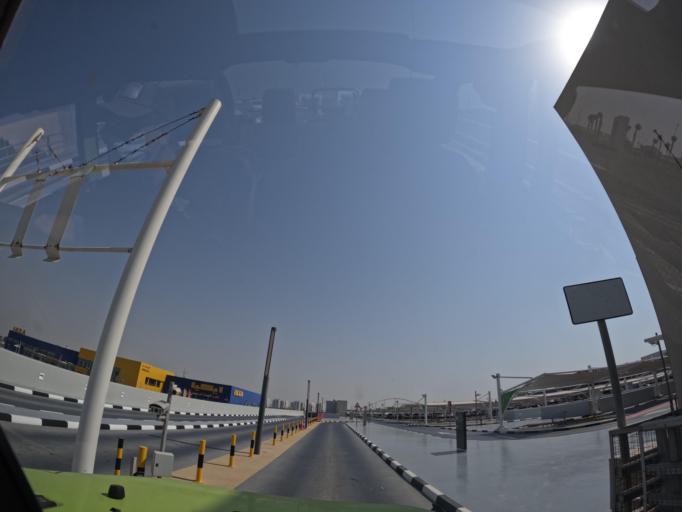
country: AE
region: Abu Dhabi
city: Abu Dhabi
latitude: 24.4908
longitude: 54.6117
